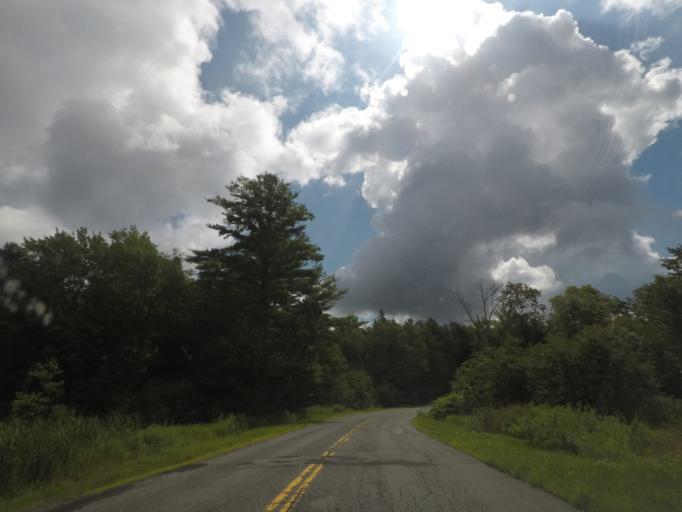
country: US
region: New York
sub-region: Rensselaer County
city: Averill Park
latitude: 42.6779
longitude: -73.4257
